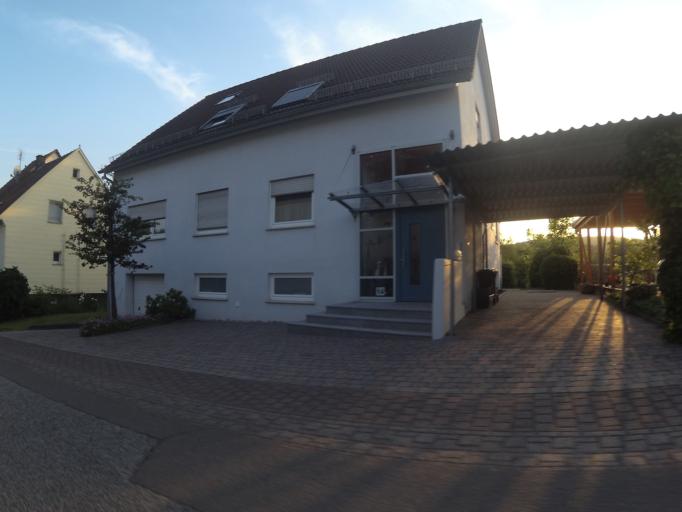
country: DE
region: Rheinland-Pfalz
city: Brucken
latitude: 49.4346
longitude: 7.3628
